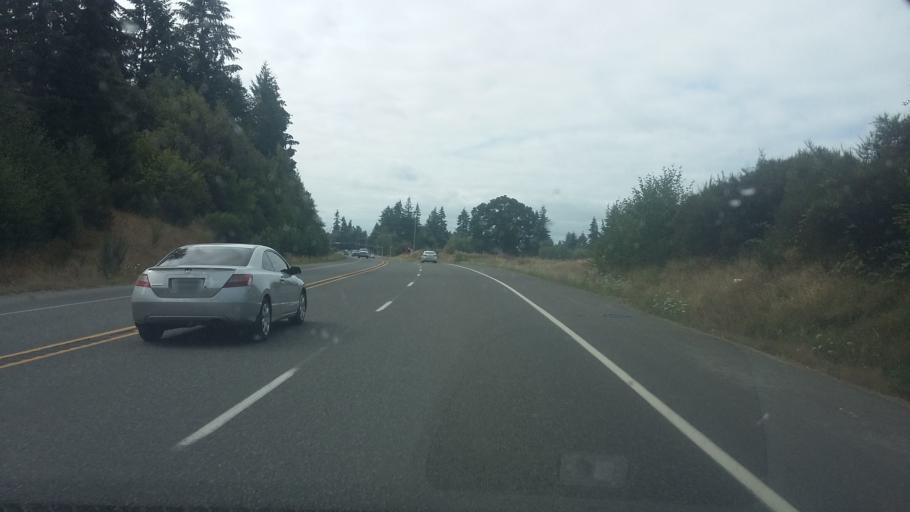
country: US
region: Washington
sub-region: Clark County
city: Battle Ground
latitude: 45.8029
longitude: -122.5495
